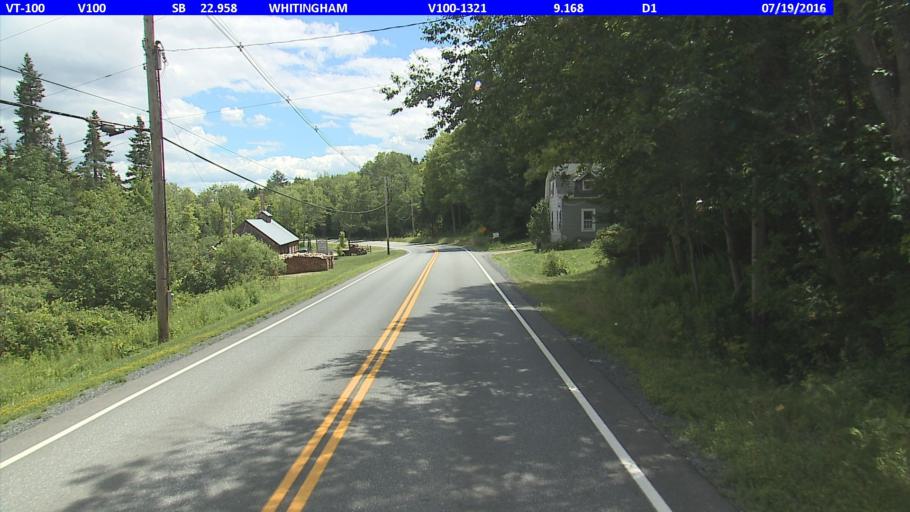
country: US
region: Vermont
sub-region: Windham County
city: Dover
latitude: 42.8112
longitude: -72.8425
